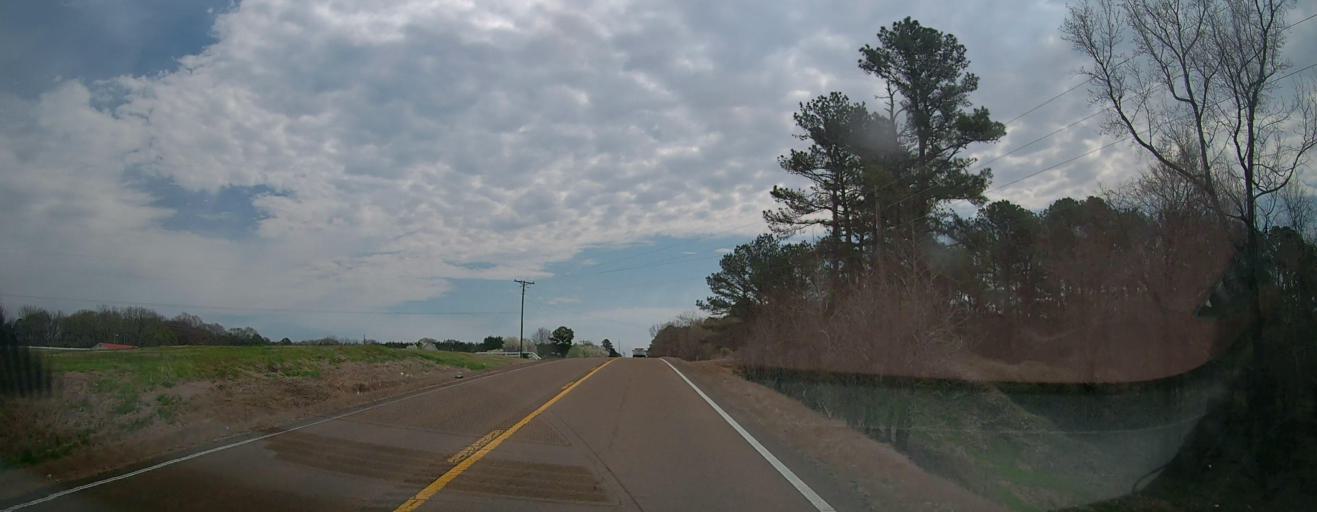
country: US
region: Mississippi
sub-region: Marshall County
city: Holly Springs
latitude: 34.8187
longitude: -89.5368
